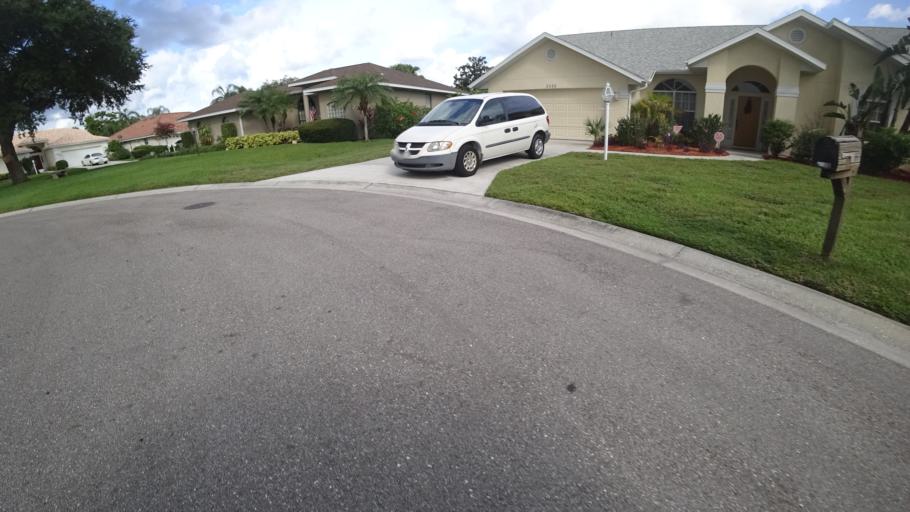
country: US
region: Florida
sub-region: Sarasota County
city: Desoto Lakes
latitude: 27.4186
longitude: -82.4852
